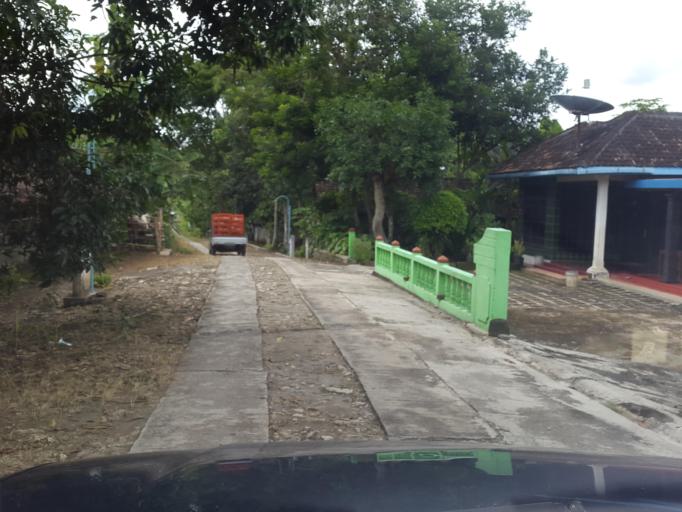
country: ID
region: Daerah Istimewa Yogyakarta
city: Wonosari
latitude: -7.8723
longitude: 110.6786
